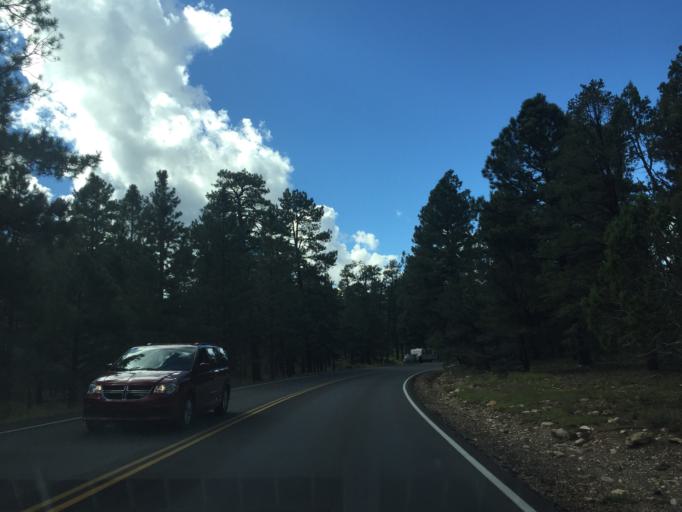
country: US
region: Arizona
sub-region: Coconino County
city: Grand Canyon
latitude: 36.0534
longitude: -112.1254
